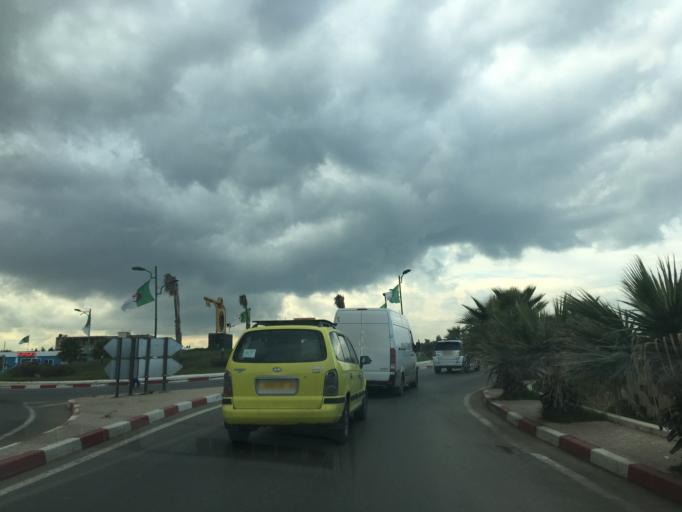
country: DZ
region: Bouira
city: Bouira
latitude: 36.3674
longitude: 3.8674
